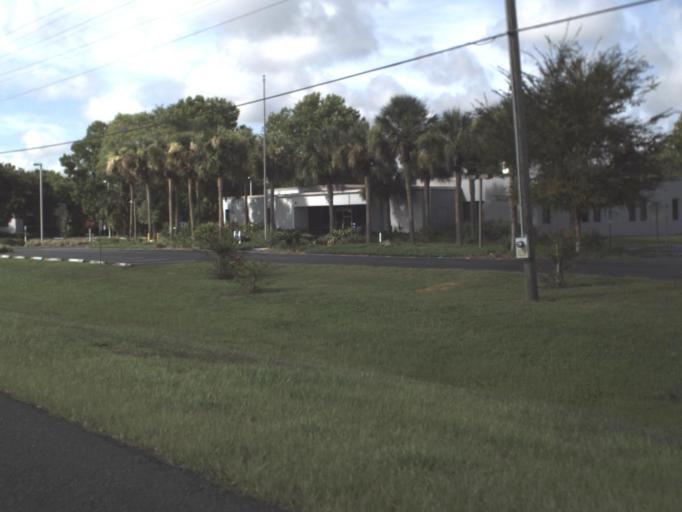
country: US
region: Florida
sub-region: Pasco County
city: Land O' Lakes
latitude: 28.2634
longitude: -82.4768
